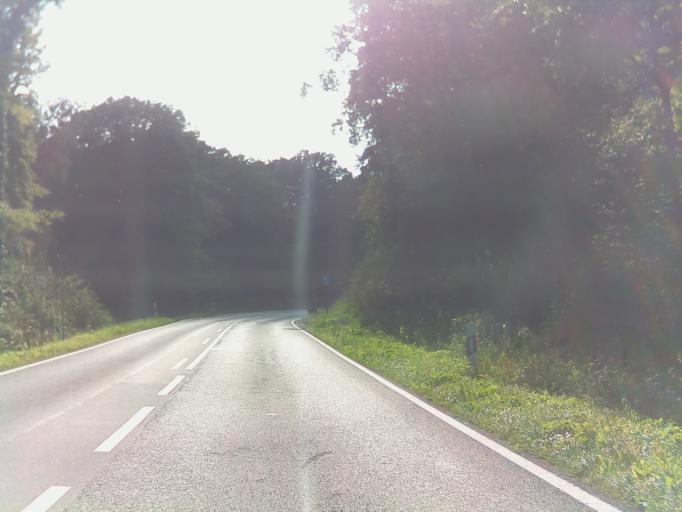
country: DE
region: Bavaria
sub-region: Regierungsbezirk Unterfranken
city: Gemunden
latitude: 50.0384
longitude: 9.7298
